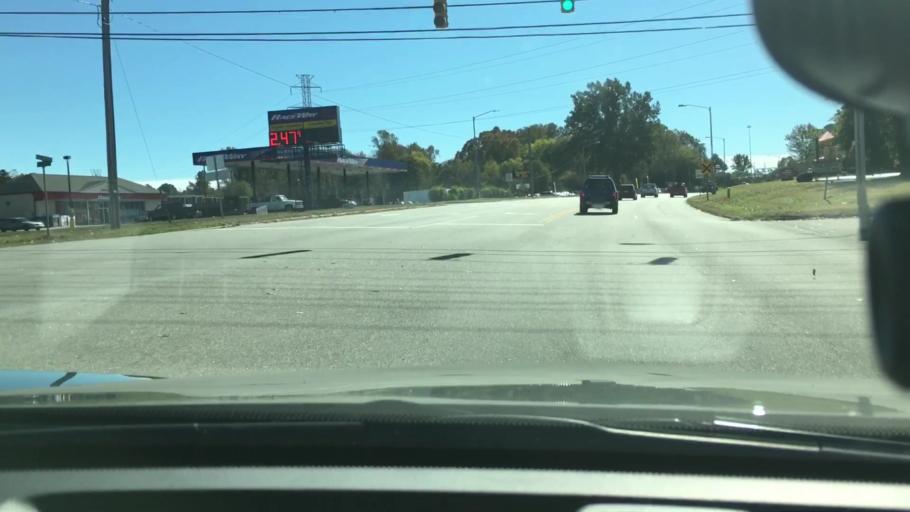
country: US
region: North Carolina
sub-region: Edgecombe County
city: Tarboro
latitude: 35.8912
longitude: -77.5491
